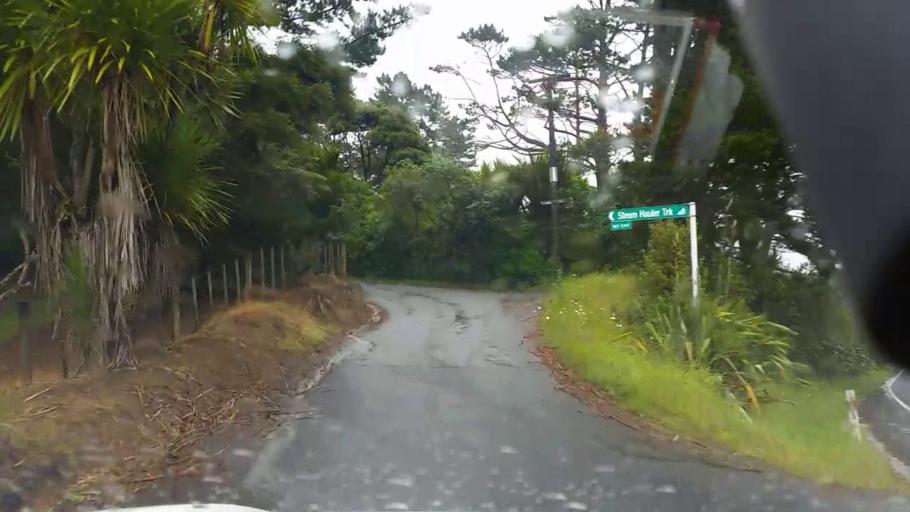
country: NZ
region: Auckland
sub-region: Auckland
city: Muriwai Beach
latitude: -36.8597
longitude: 174.5212
